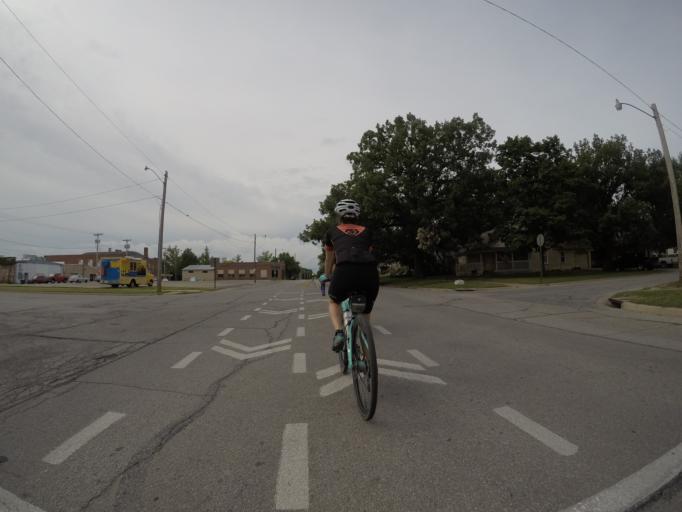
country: US
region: Kansas
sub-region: Franklin County
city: Ottawa
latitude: 38.6129
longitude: -95.2700
